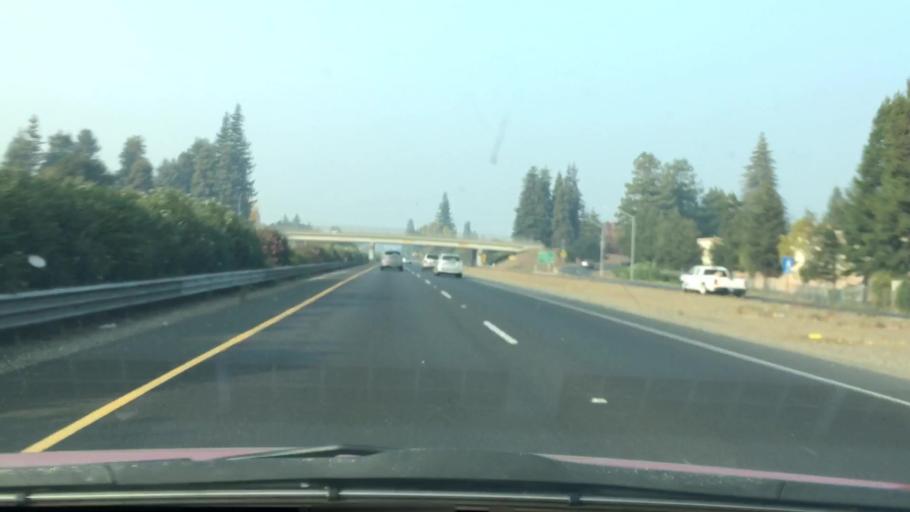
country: US
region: California
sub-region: Napa County
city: Napa
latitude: 38.3049
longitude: -122.3041
